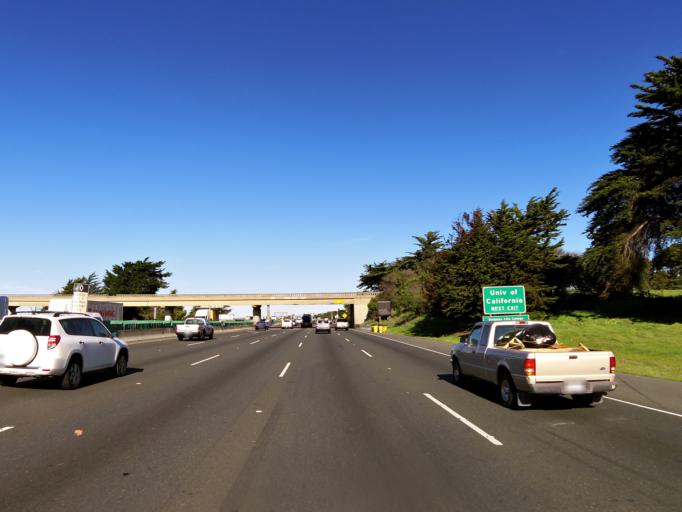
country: US
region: California
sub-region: Alameda County
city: Emeryville
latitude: 37.8480
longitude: -122.2985
